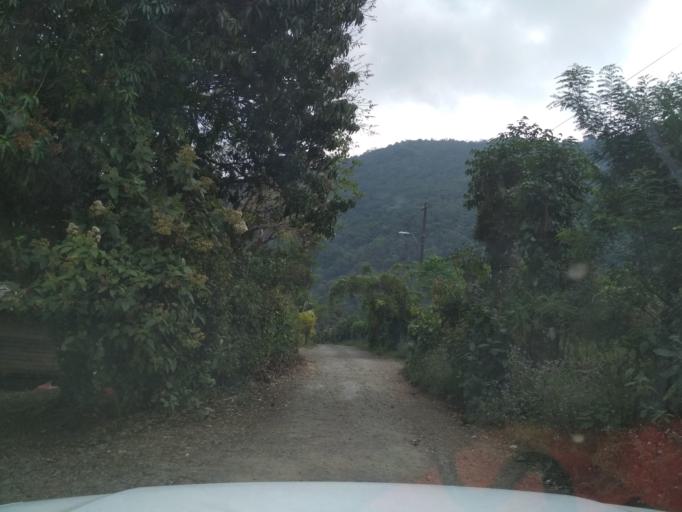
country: MX
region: Veracruz
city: Cuautlapan
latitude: 18.8664
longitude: -97.0153
